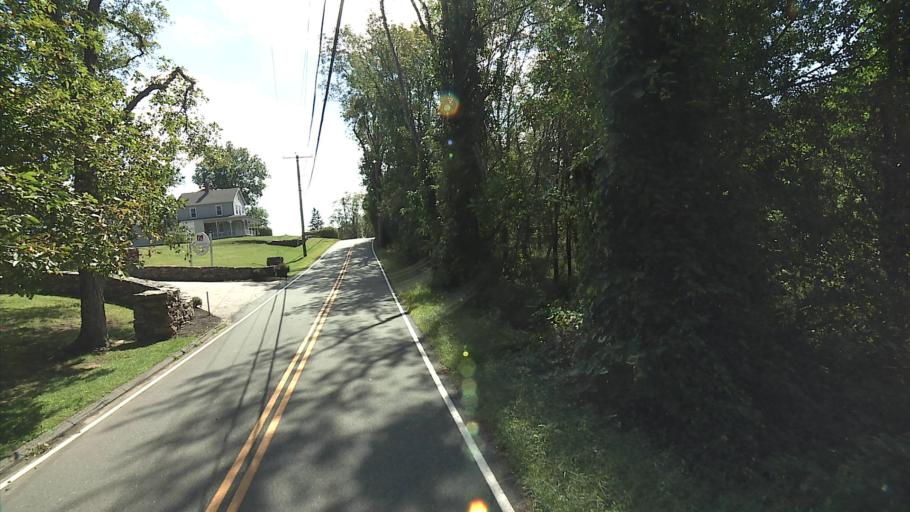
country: US
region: Connecticut
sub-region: Middlesex County
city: East Haddam
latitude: 41.4405
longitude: -72.4348
